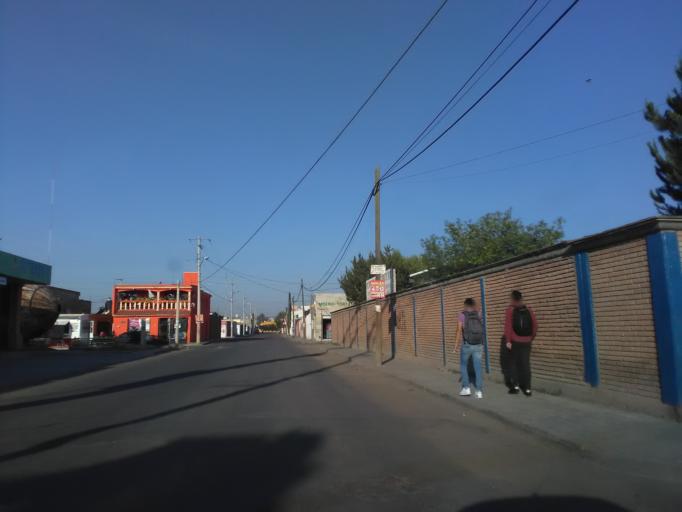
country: MX
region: Durango
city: Victoria de Durango
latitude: 24.0576
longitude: -104.6206
